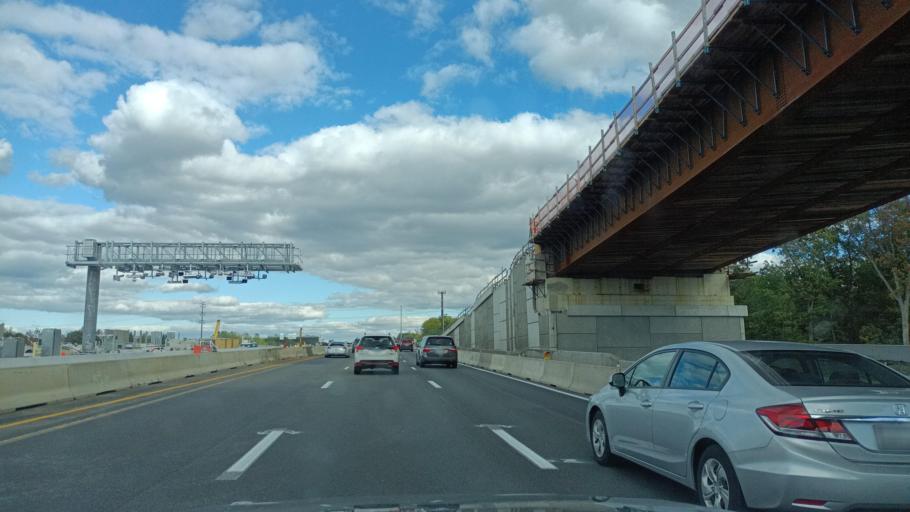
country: US
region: Virginia
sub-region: Fairfax County
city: Greenbriar
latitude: 38.8498
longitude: -77.4054
